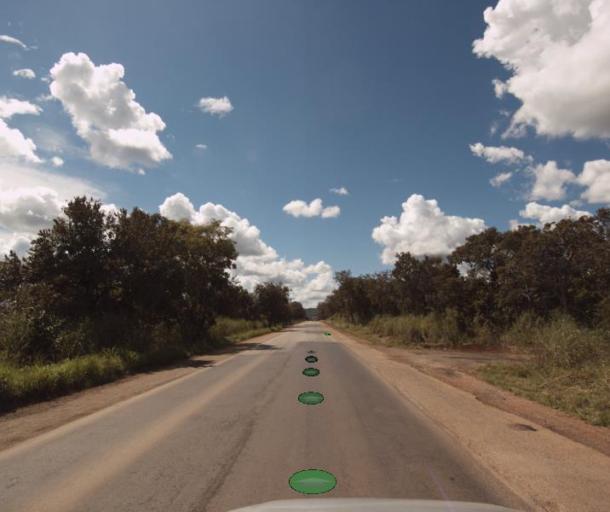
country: BR
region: Goias
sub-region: Porangatu
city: Porangatu
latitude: -13.6870
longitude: -49.0229
